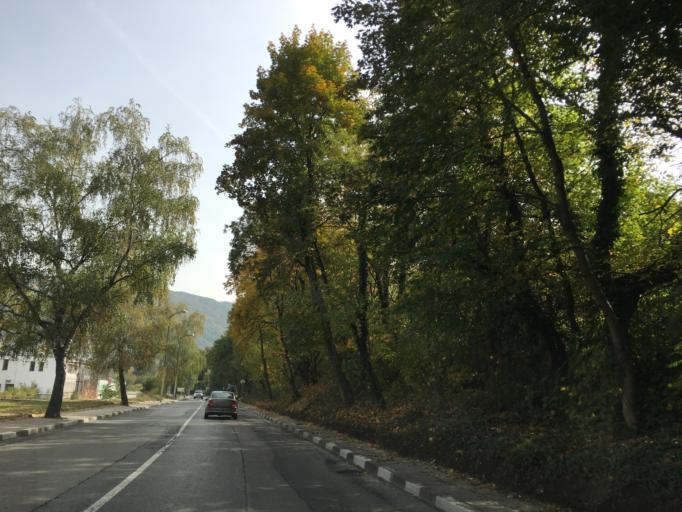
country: BG
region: Sofia-Capital
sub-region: Stolichna Obshtina
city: Sofia
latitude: 42.5974
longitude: 23.4072
